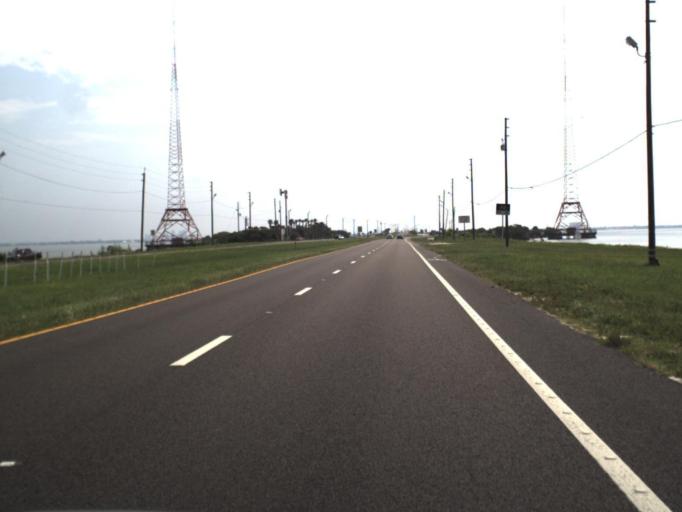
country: US
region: Florida
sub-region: Pinellas County
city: Gandy
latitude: 27.8762
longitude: -82.5940
